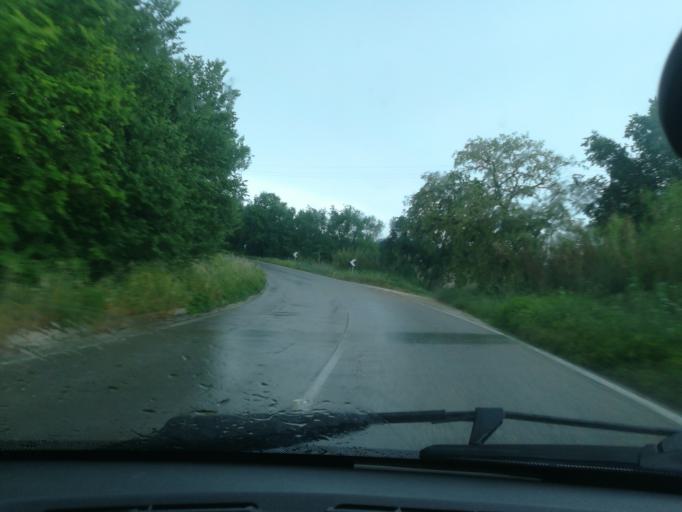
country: IT
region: The Marches
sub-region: Provincia di Macerata
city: Pollenza
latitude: 43.2874
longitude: 13.3818
